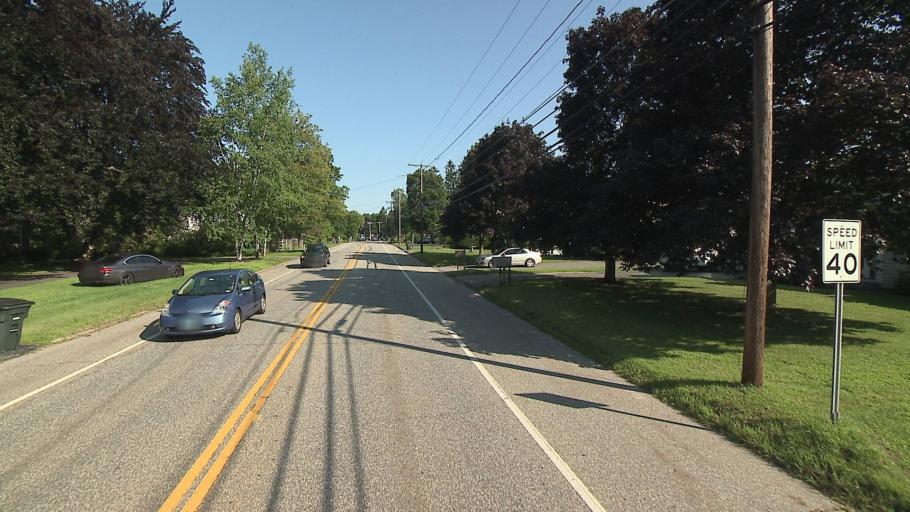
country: US
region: Connecticut
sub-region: Litchfield County
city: Torrington
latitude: 41.8032
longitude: -73.0924
